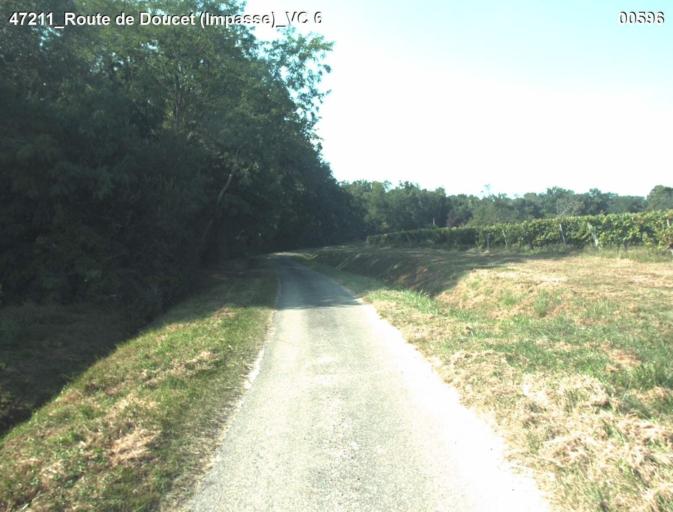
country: FR
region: Midi-Pyrenees
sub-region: Departement du Gers
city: Montreal
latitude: 44.0175
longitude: 0.2013
